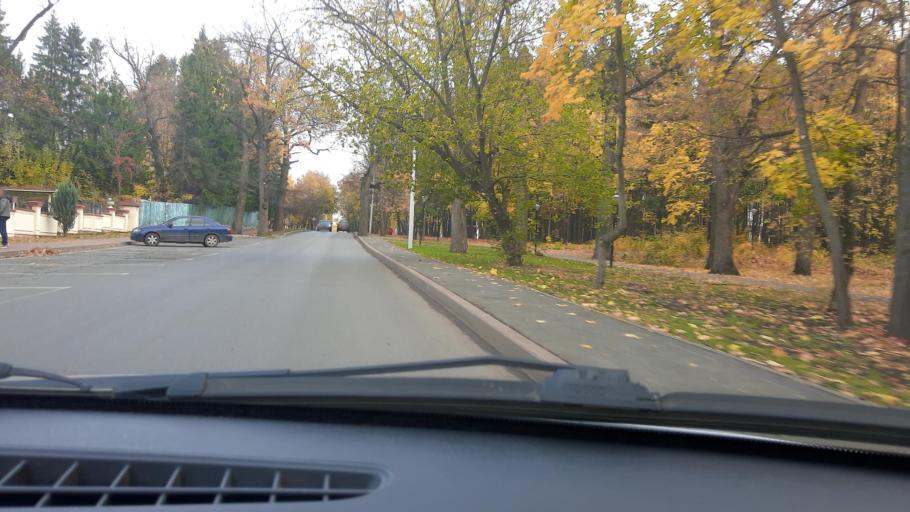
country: RU
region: Bashkortostan
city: Ufa
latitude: 54.7705
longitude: 56.0183
